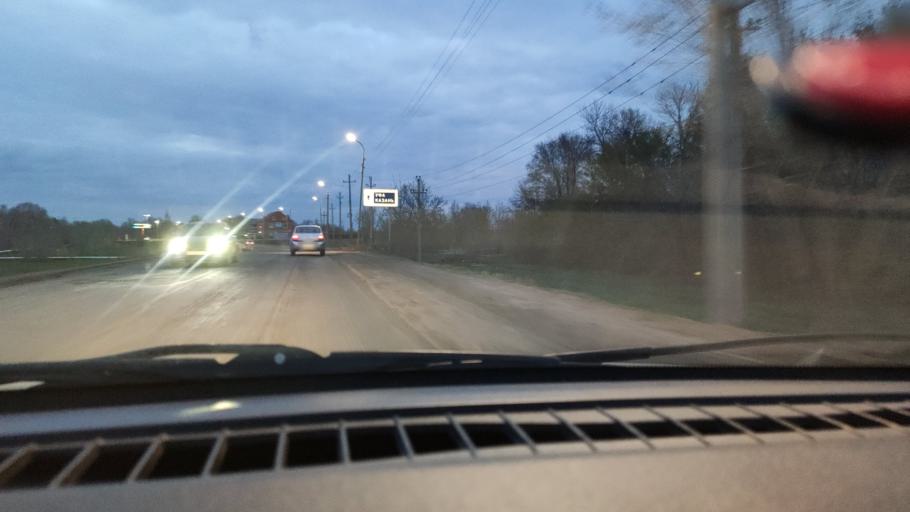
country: RU
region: Orenburg
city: Tatarskaya Kargala
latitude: 51.8680
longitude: 55.1421
